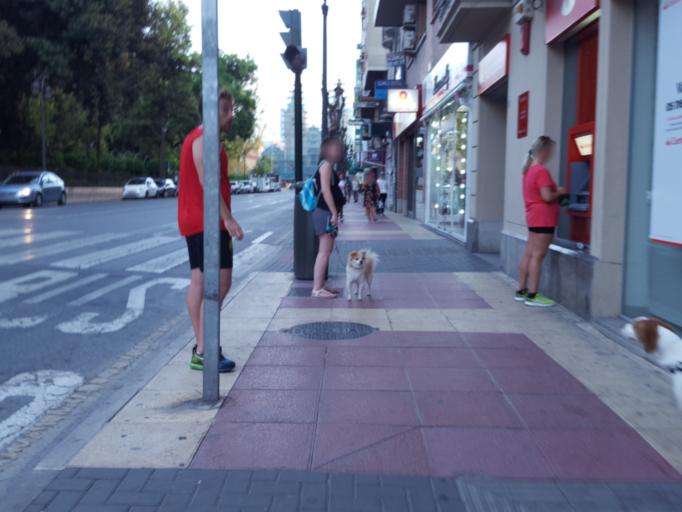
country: ES
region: Murcia
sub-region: Murcia
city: Murcia
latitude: 37.9813
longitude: -1.1310
